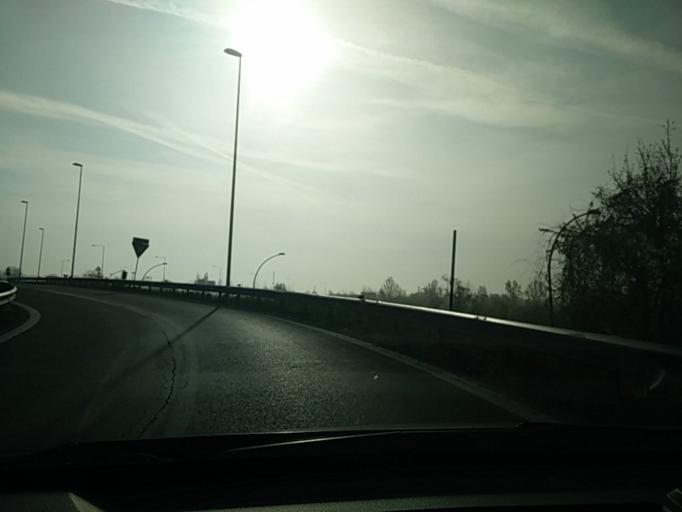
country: IT
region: Emilia-Romagna
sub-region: Provincia di Bologna
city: Bologna
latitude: 44.5214
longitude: 11.3642
